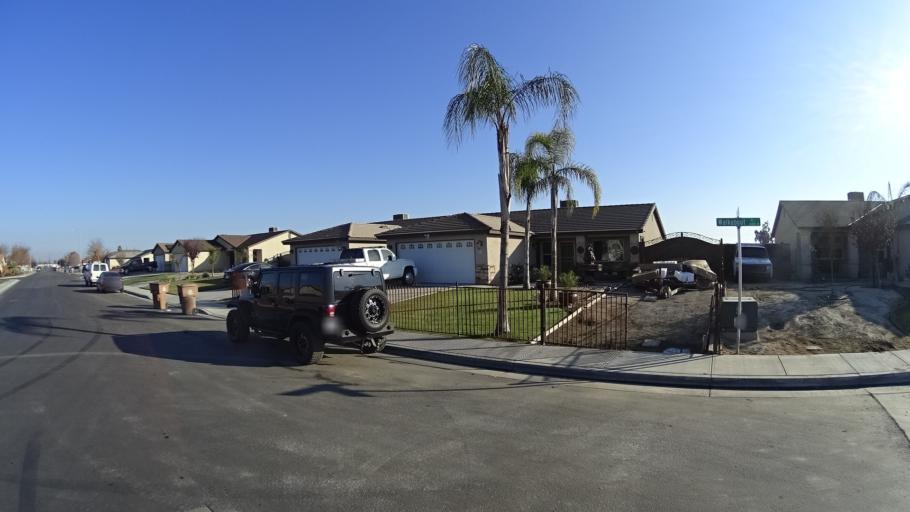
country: US
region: California
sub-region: Kern County
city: Greenfield
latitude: 35.3003
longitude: -119.0061
